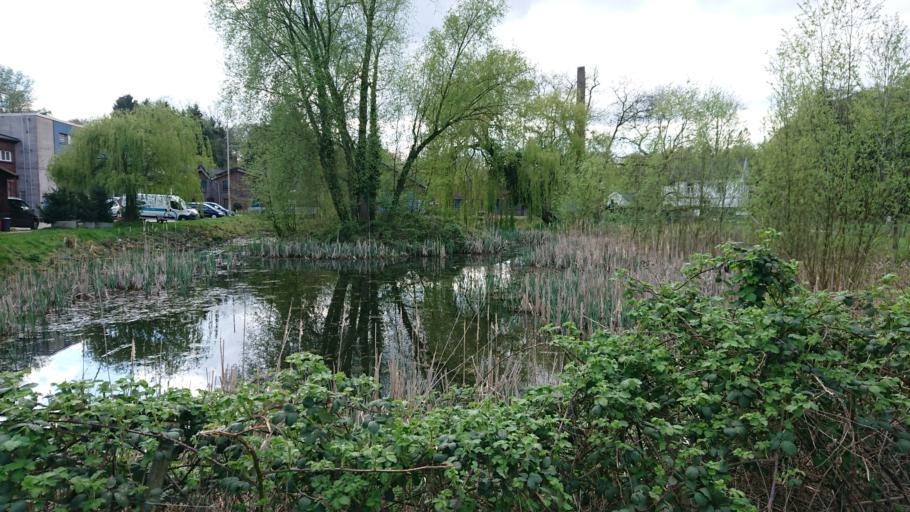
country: DE
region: North Rhine-Westphalia
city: Opladen
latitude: 51.0317
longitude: 7.0564
